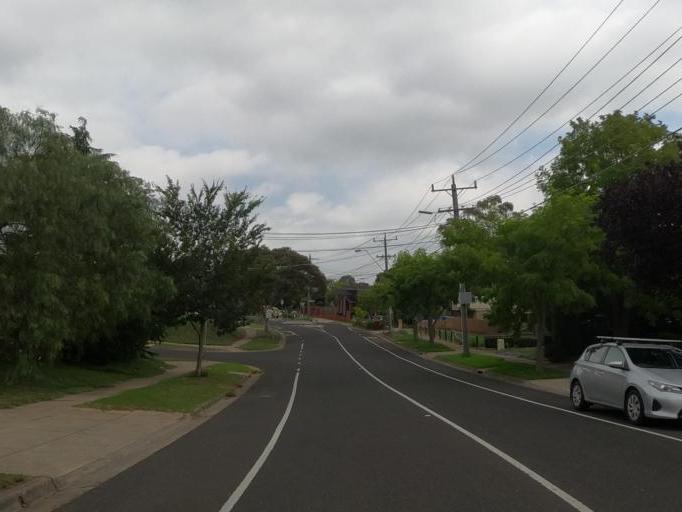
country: AU
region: Victoria
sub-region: Hume
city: Attwood
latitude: -37.6698
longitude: 144.8996
